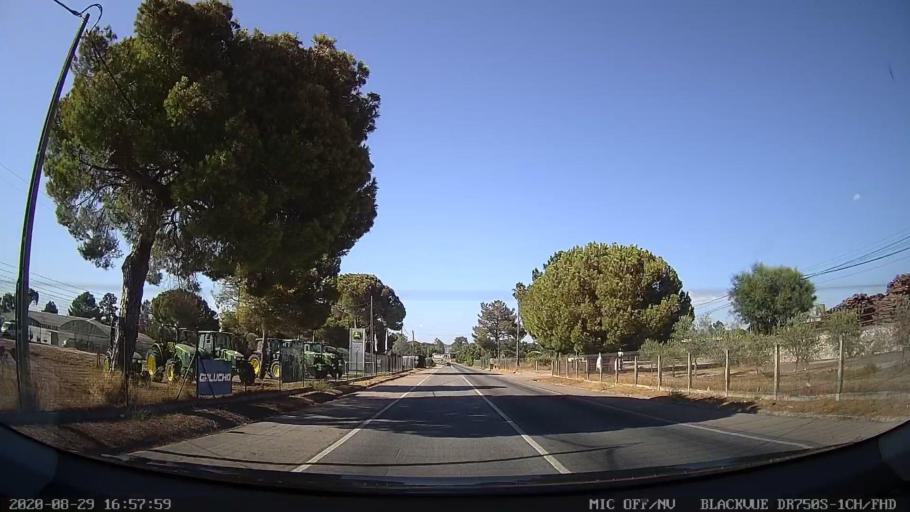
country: PT
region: Setubal
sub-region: Alcacer do Sal
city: Alcacer do Sal
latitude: 38.3992
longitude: -8.5147
